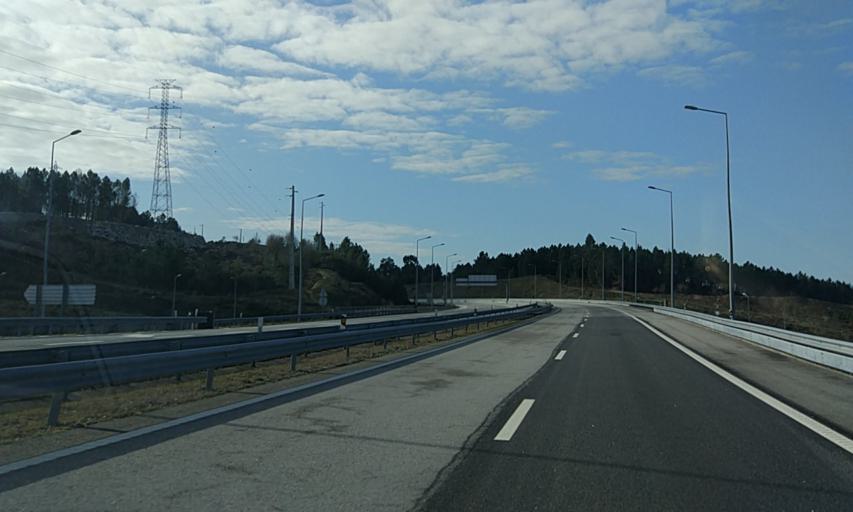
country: PT
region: Viseu
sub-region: Castro Daire
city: Castro Daire
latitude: 40.8219
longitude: -7.9360
